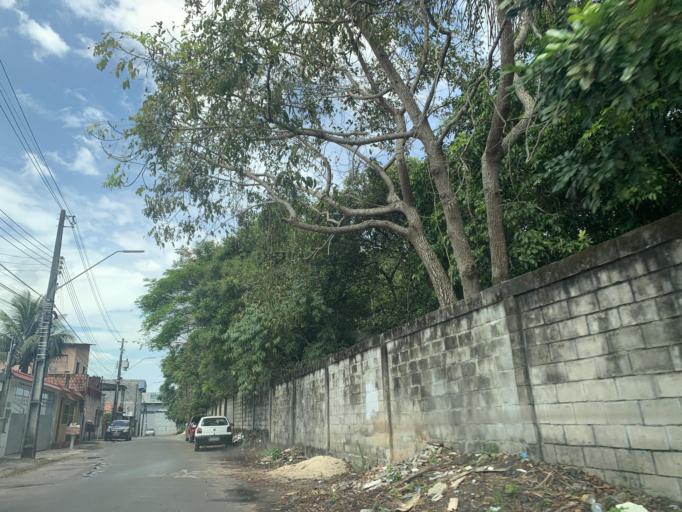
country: BR
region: Amazonas
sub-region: Manaus
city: Manaus
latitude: -3.0939
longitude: -59.9534
